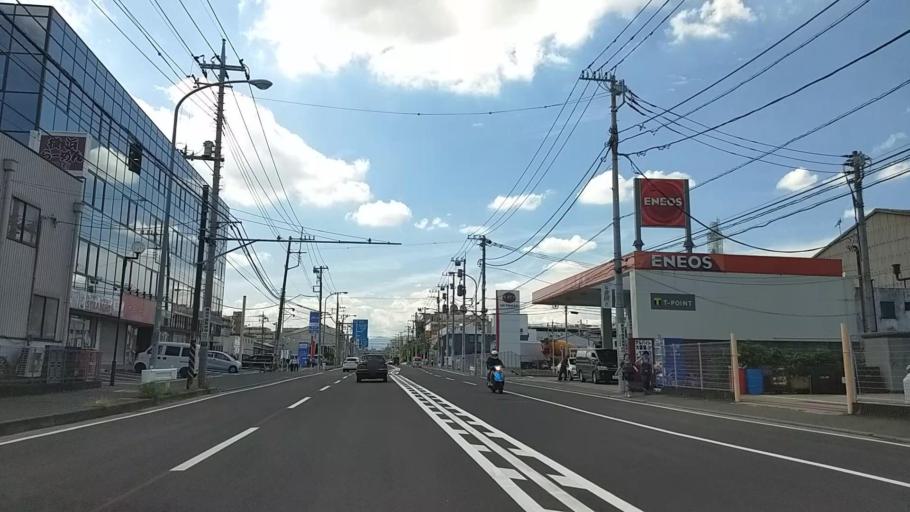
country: JP
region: Kanagawa
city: Yokohama
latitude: 35.5168
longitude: 139.5716
